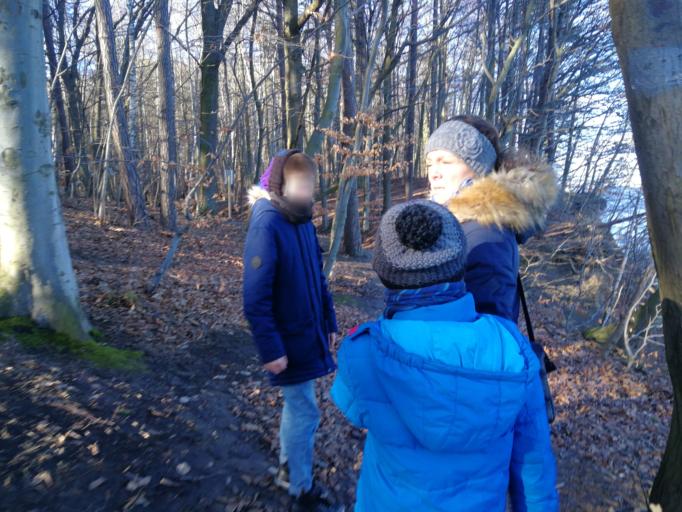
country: PL
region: Pomeranian Voivodeship
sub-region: Sopot
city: Sopot
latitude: 54.4856
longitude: 18.5683
